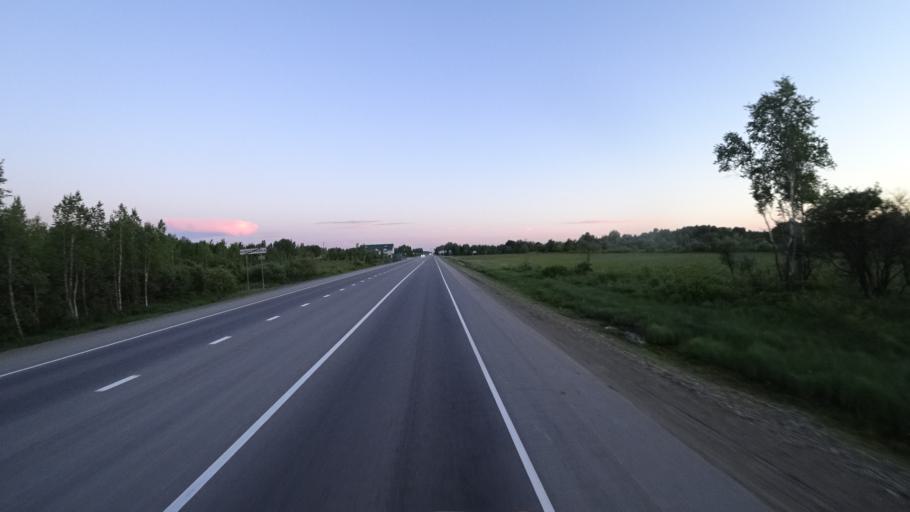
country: RU
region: Khabarovsk Krai
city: Khor
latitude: 47.8449
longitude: 134.9577
